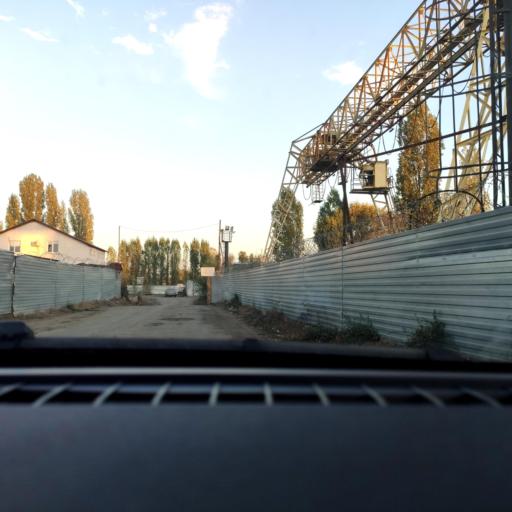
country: RU
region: Voronezj
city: Maslovka
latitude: 51.6402
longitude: 39.2855
